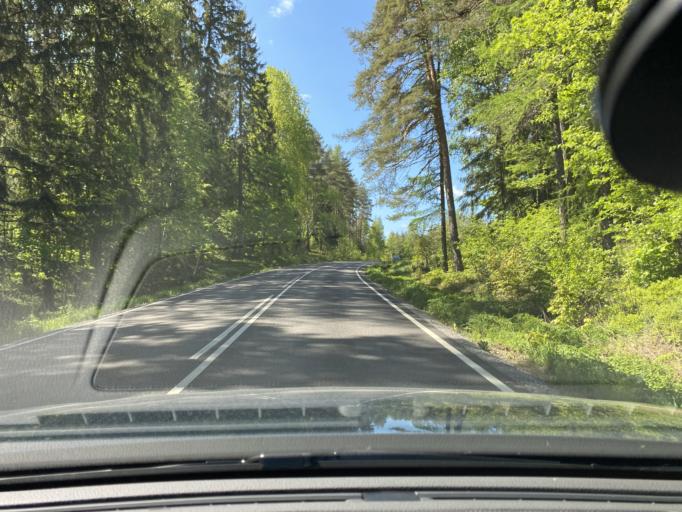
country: FI
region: Varsinais-Suomi
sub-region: Salo
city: Halikko
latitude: 60.3632
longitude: 22.9898
